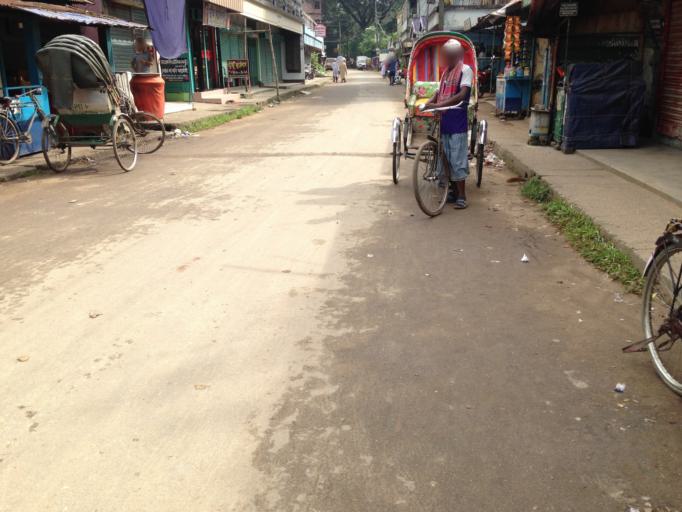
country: IN
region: Tripura
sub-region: Dhalai
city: Kamalpur
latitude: 24.3100
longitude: 91.7274
